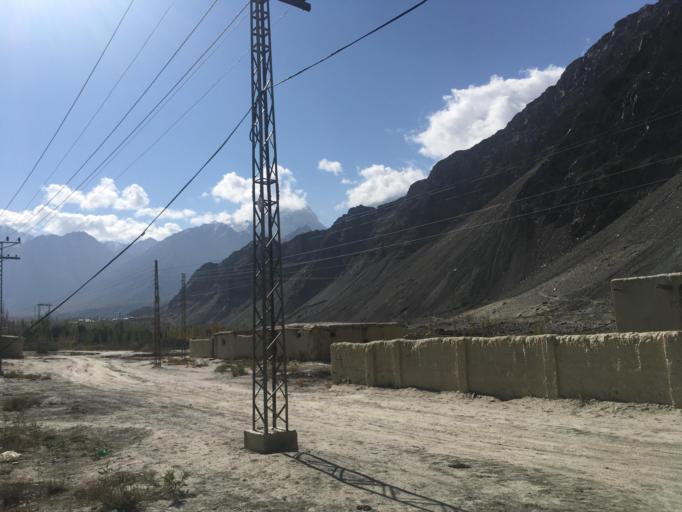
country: PK
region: Gilgit-Baltistan
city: Skardu
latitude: 35.3281
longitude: 75.5250
